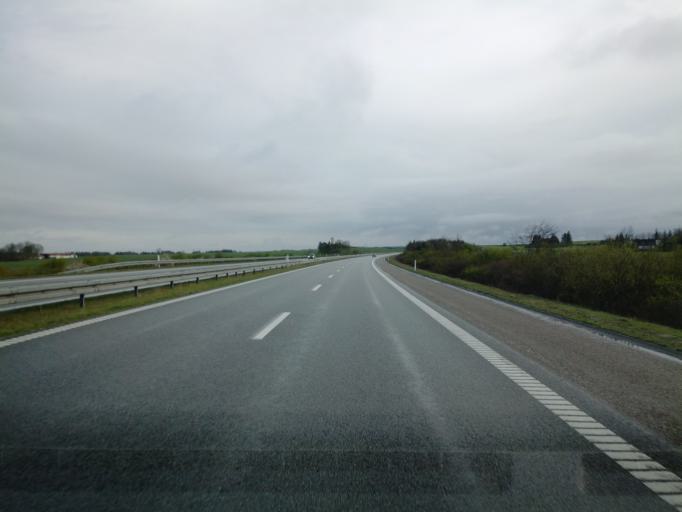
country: DK
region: North Denmark
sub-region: Bronderslev Kommune
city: Hjallerup
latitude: 57.1907
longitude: 10.1981
